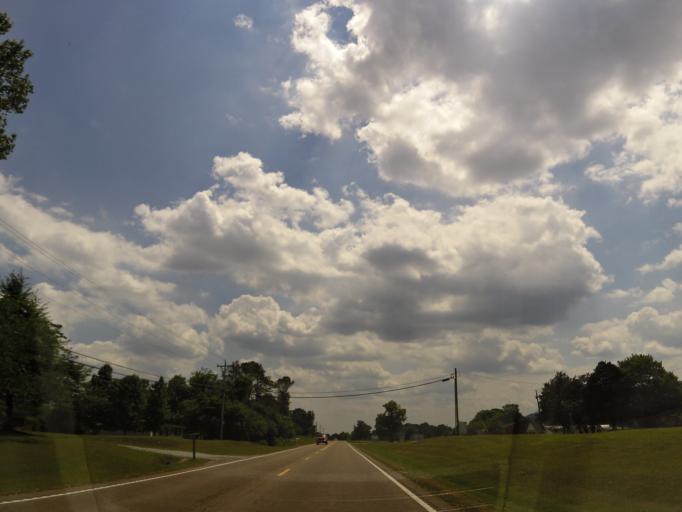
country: US
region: Tennessee
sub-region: Bledsoe County
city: Pikeville
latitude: 35.5568
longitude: -85.2504
